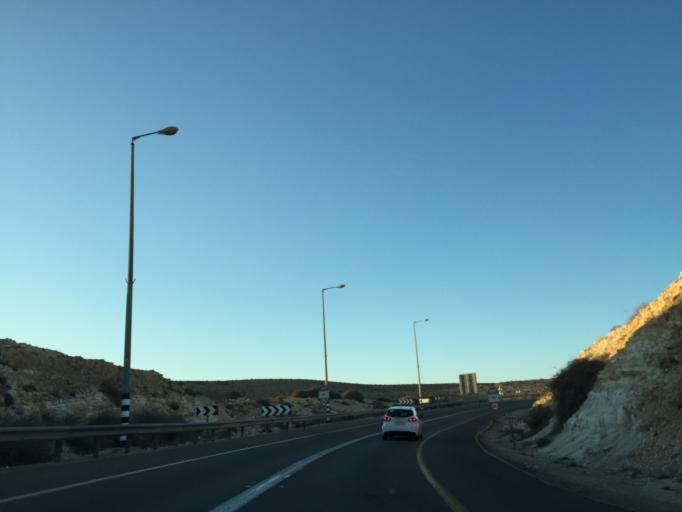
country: IL
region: Southern District
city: Midreshet Ben-Gurion
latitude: 30.8835
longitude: 34.7935
